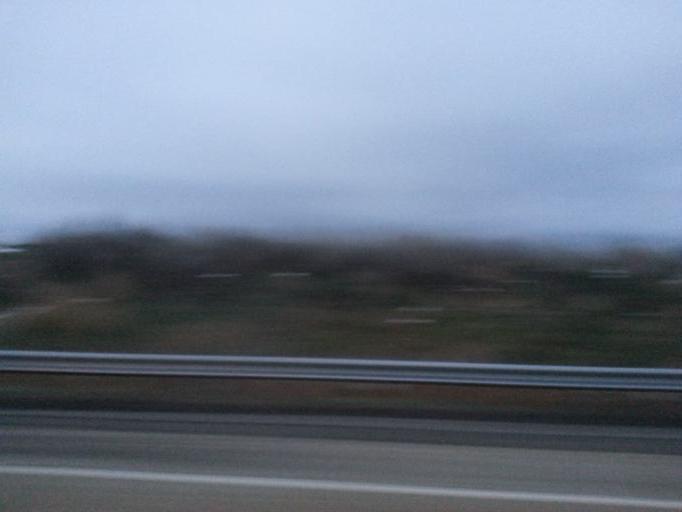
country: US
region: Iowa
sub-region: Black Hawk County
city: Elk Run Heights
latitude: 42.4448
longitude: -92.1891
